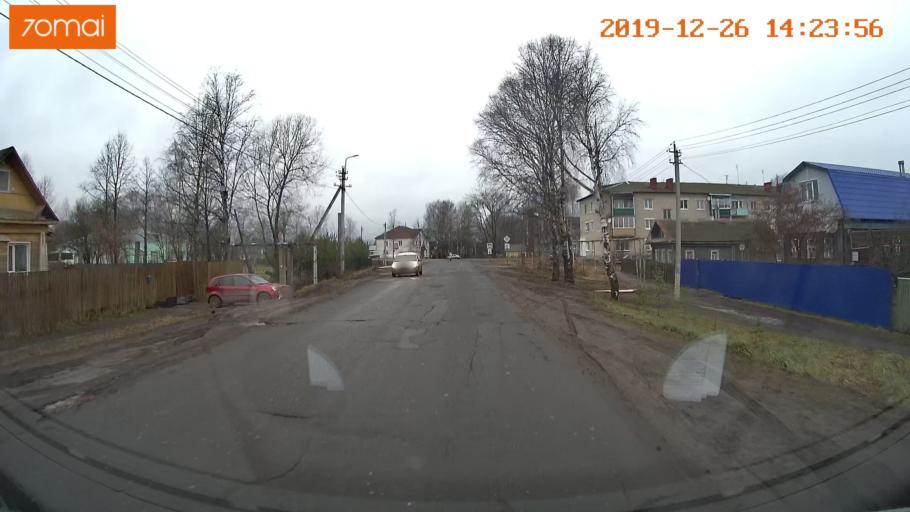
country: RU
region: Jaroslavl
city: Poshekhon'ye
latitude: 58.4986
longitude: 39.1113
